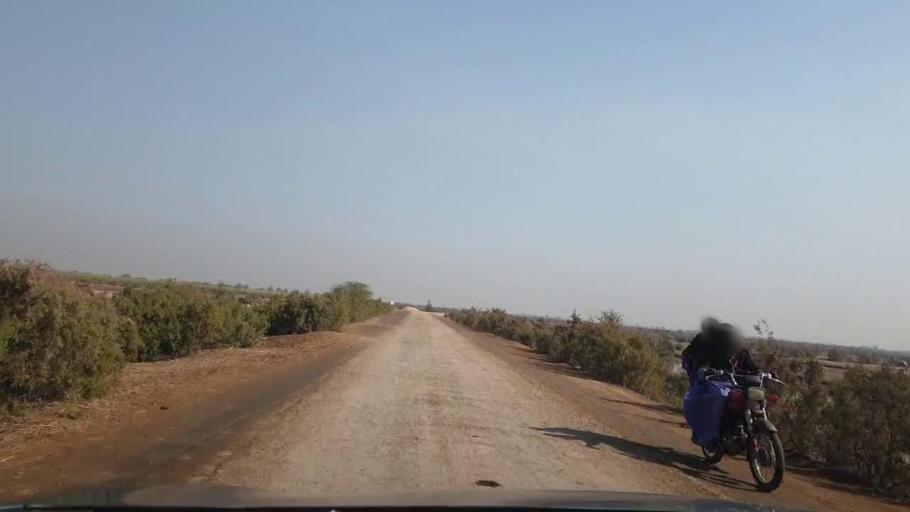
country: PK
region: Sindh
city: Berani
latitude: 25.6437
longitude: 68.8730
